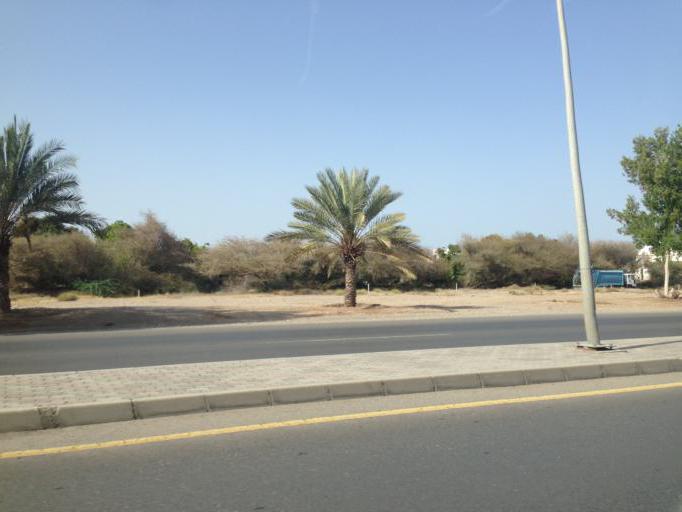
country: OM
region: Muhafazat Masqat
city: As Sib al Jadidah
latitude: 23.6132
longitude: 58.2325
